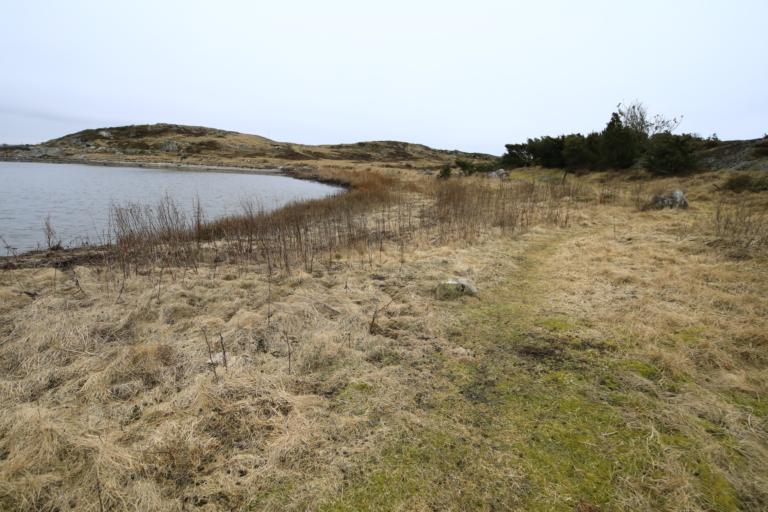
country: SE
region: Halland
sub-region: Kungsbacka Kommun
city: Frillesas
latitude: 57.2470
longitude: 12.1199
